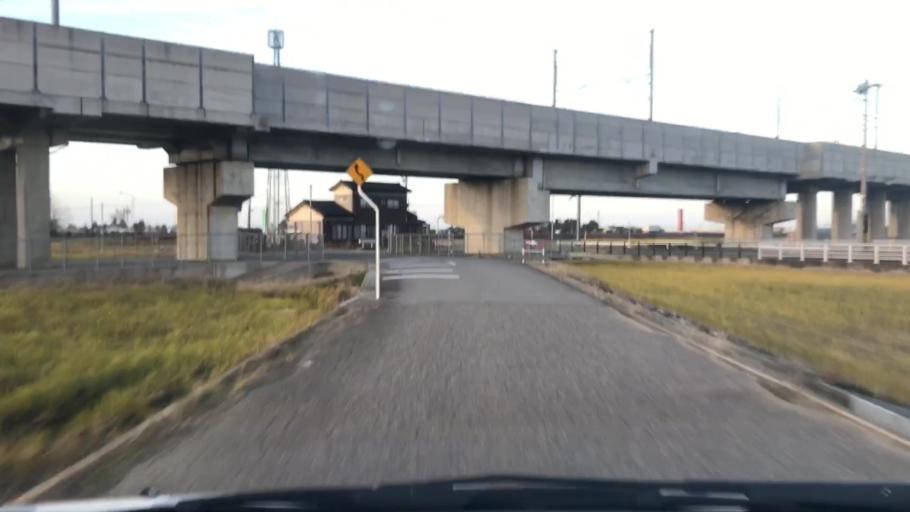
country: JP
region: Toyama
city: Namerikawa
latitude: 36.7317
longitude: 137.3357
